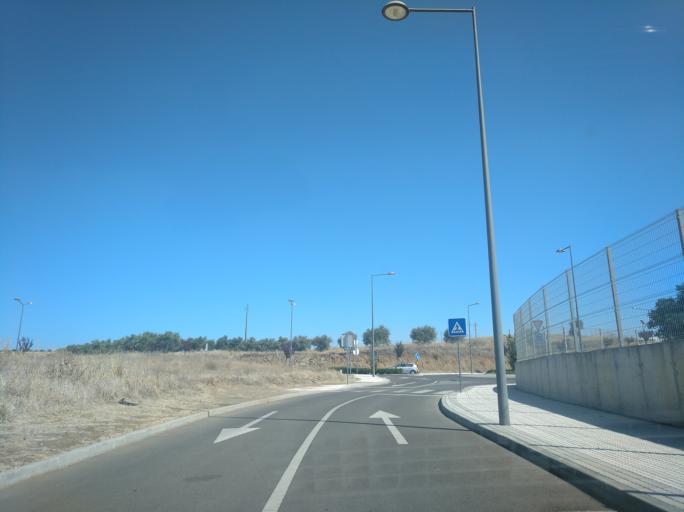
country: PT
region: Portalegre
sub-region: Campo Maior
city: Campo Maior
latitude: 39.0192
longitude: -7.0708
